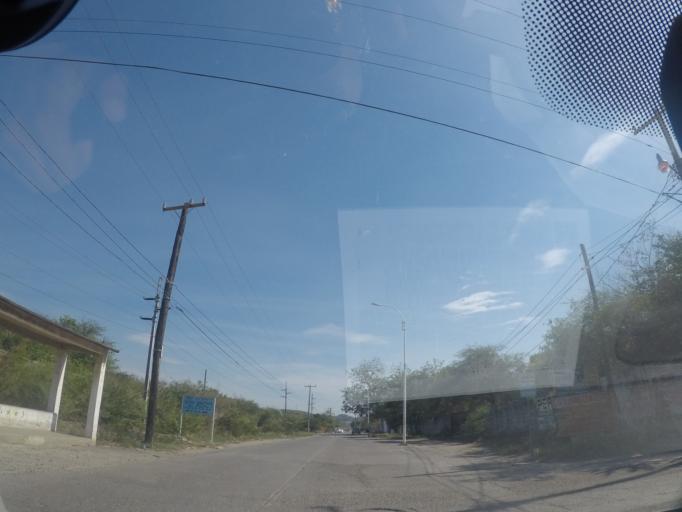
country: MX
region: Oaxaca
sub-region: Salina Cruz
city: Salina Cruz
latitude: 16.2126
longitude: -95.1938
